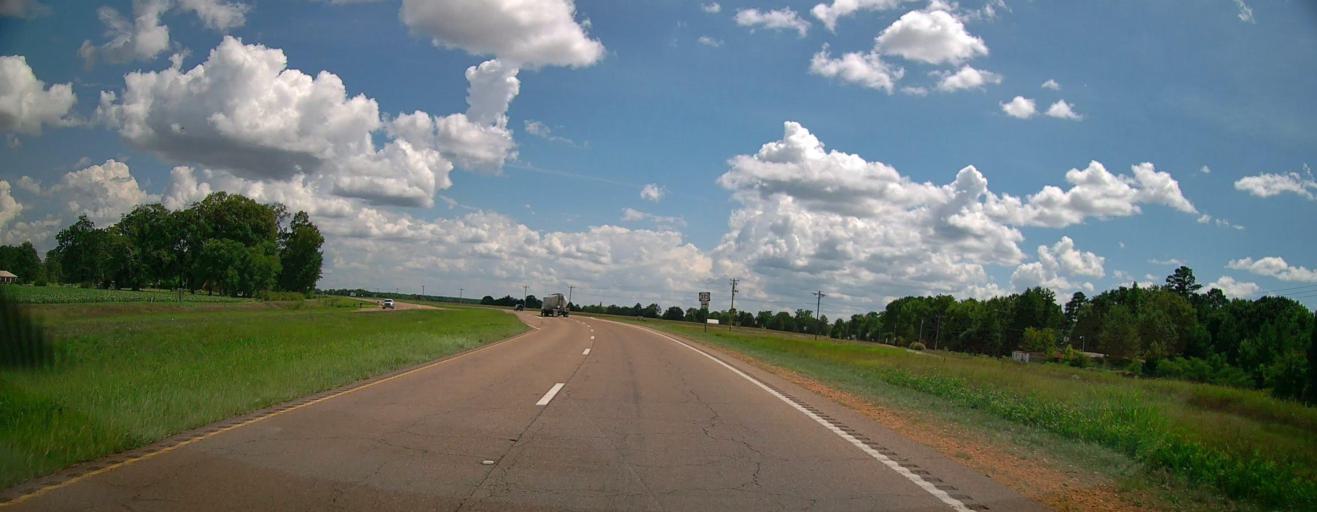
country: US
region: Mississippi
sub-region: Lowndes County
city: Columbus Air Force Base
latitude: 33.7145
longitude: -88.4513
